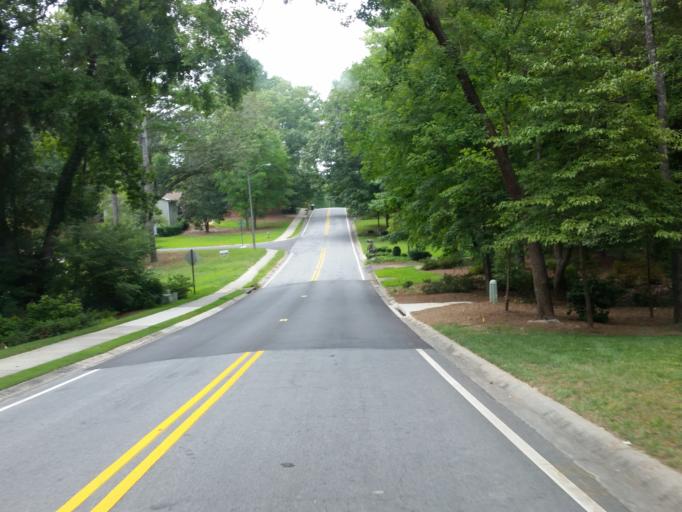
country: US
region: Georgia
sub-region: Fulton County
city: Sandy Springs
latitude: 33.9637
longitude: -84.4451
